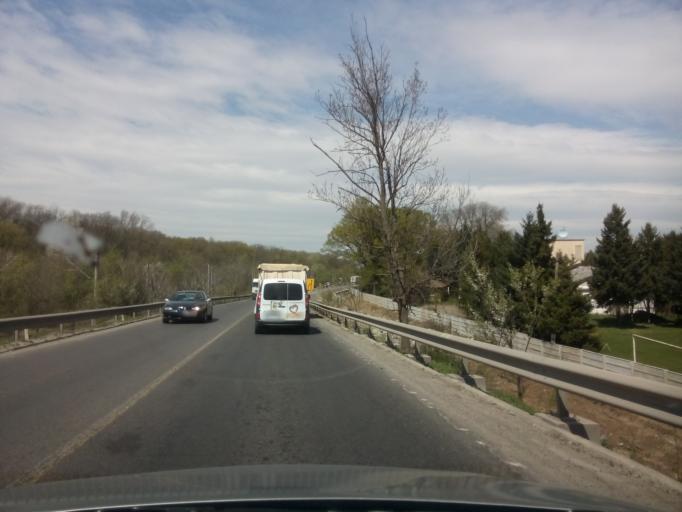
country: RO
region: Ilfov
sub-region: Comuna Pantelimon
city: Pantelimon
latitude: 44.4752
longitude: 26.2294
